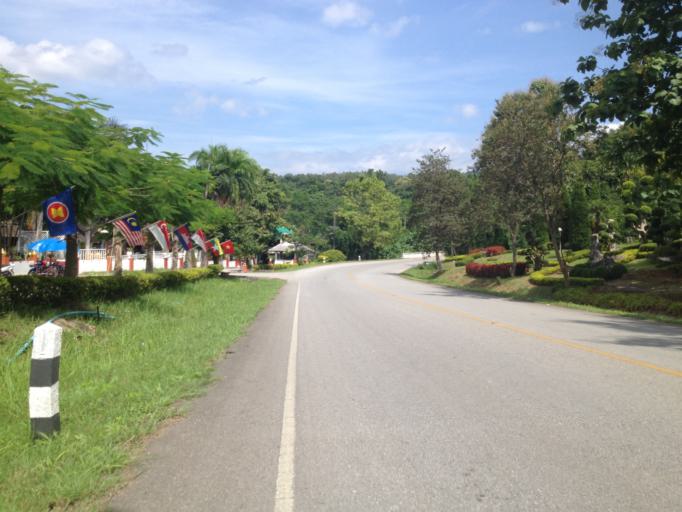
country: TH
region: Chiang Mai
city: Hang Dong
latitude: 18.7768
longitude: 98.8537
